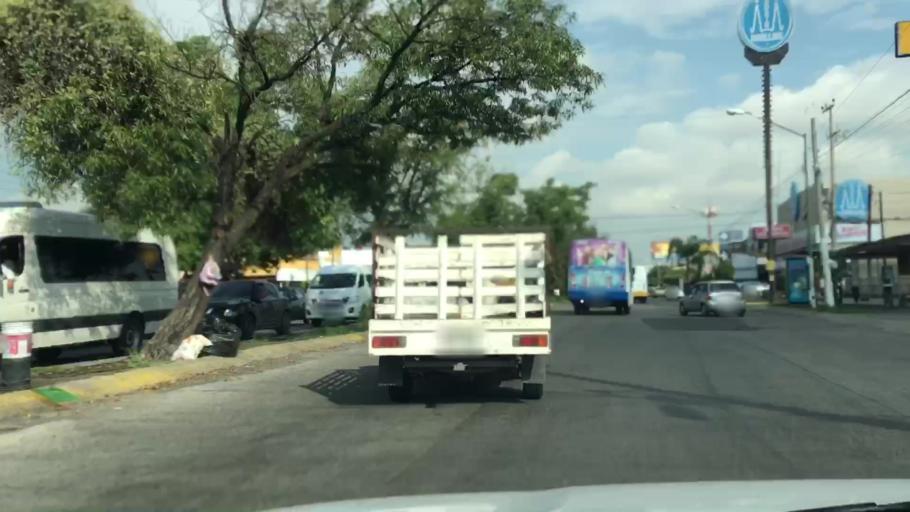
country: MX
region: Jalisco
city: Guadalajara
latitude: 20.6343
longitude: -103.4260
